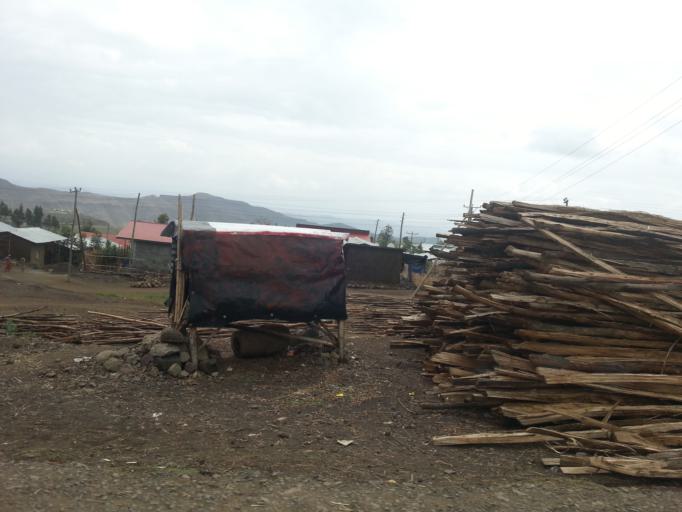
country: ET
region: Amhara
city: Lalibela
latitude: 12.0200
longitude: 39.0519
